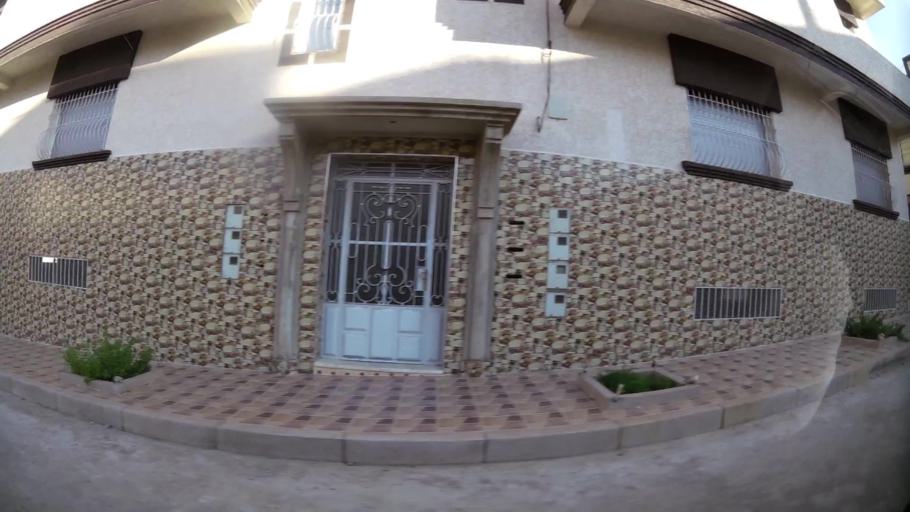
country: MA
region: Oriental
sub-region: Oujda-Angad
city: Oujda
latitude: 34.6999
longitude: -1.8994
